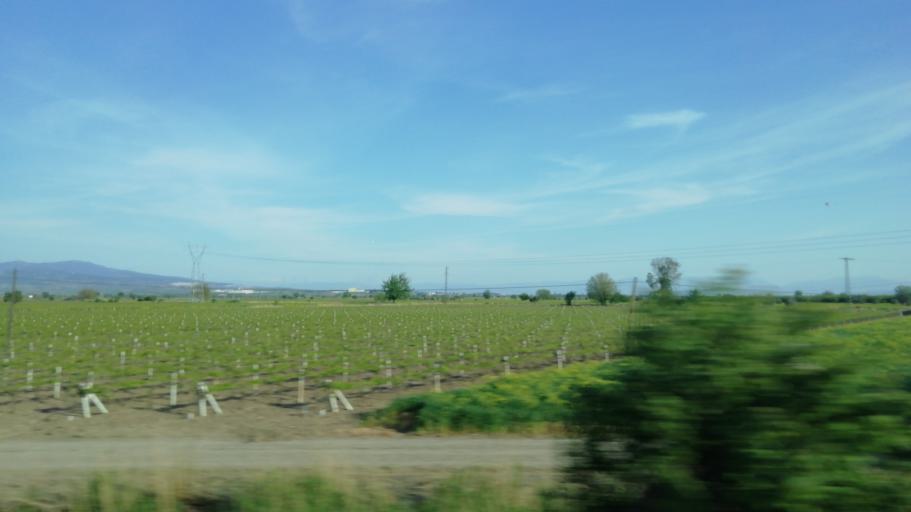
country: TR
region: Manisa
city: Saruhanli
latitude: 38.7187
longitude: 27.5577
